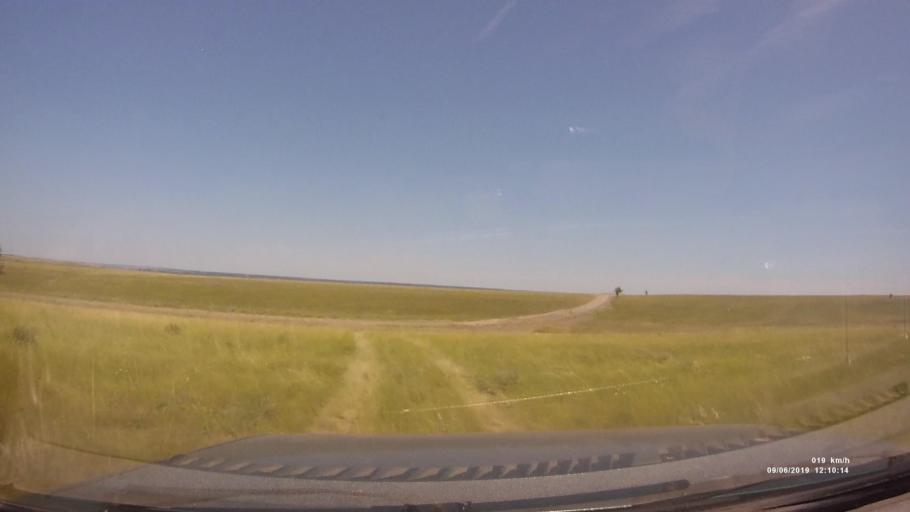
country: RU
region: Rostov
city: Staraya Stanitsa
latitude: 48.2498
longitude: 40.3389
